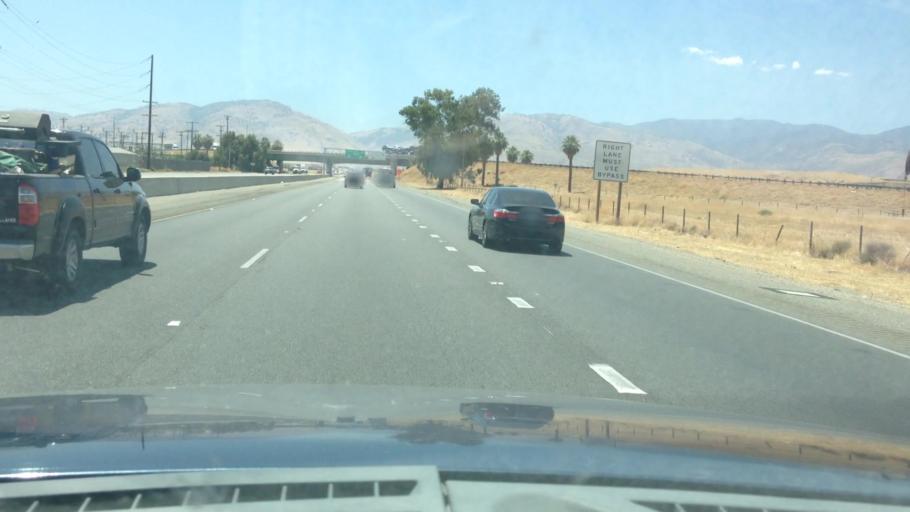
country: US
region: California
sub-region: Kern County
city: Frazier Park
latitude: 35.0218
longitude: -118.9566
